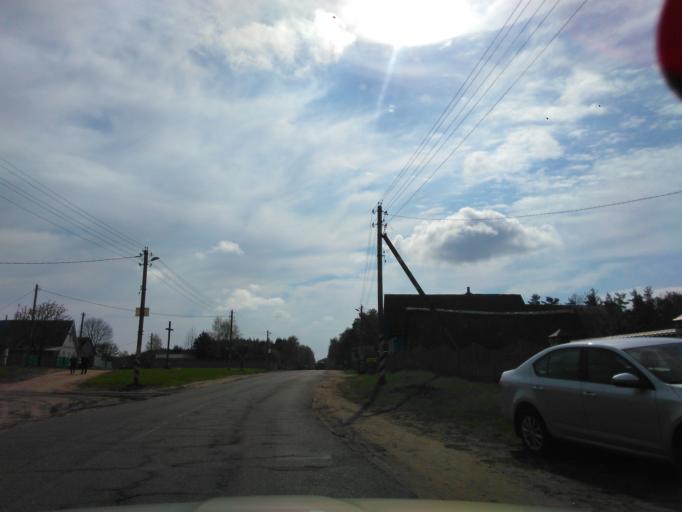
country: BY
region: Minsk
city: Rakaw
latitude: 53.9669
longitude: 27.0658
